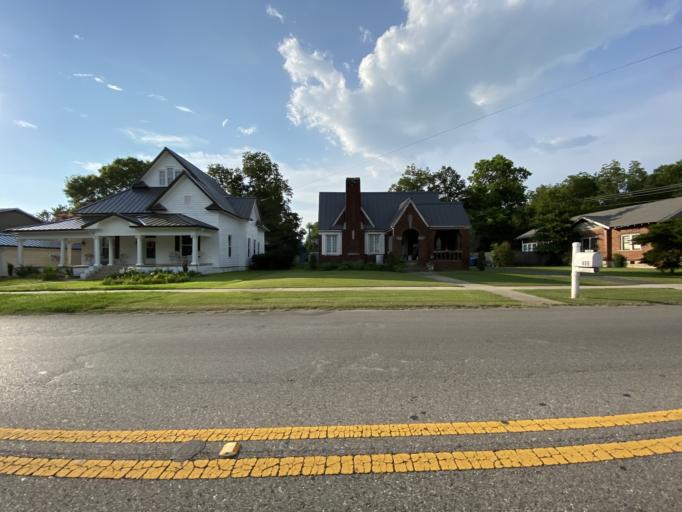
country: US
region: Alabama
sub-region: Morgan County
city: Hartselle
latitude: 34.4453
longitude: -86.9291
